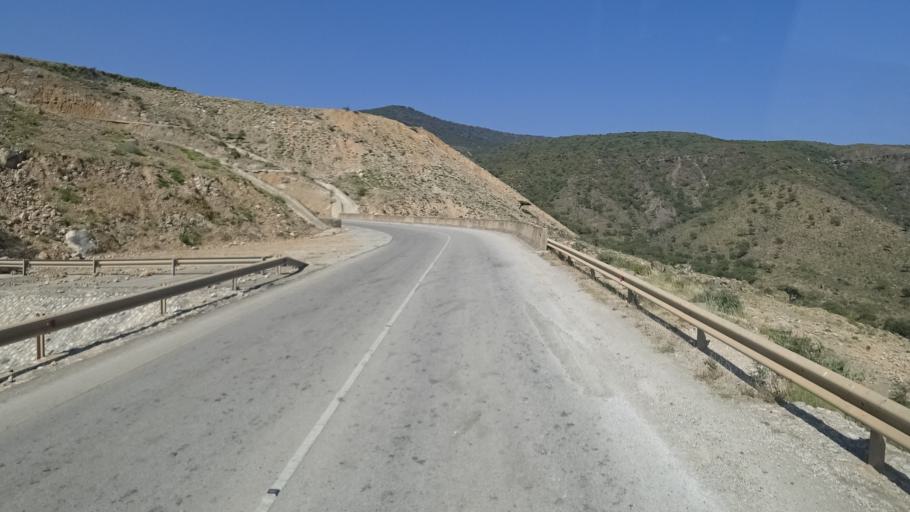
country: OM
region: Zufar
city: Salalah
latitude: 17.0461
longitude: 54.6133
